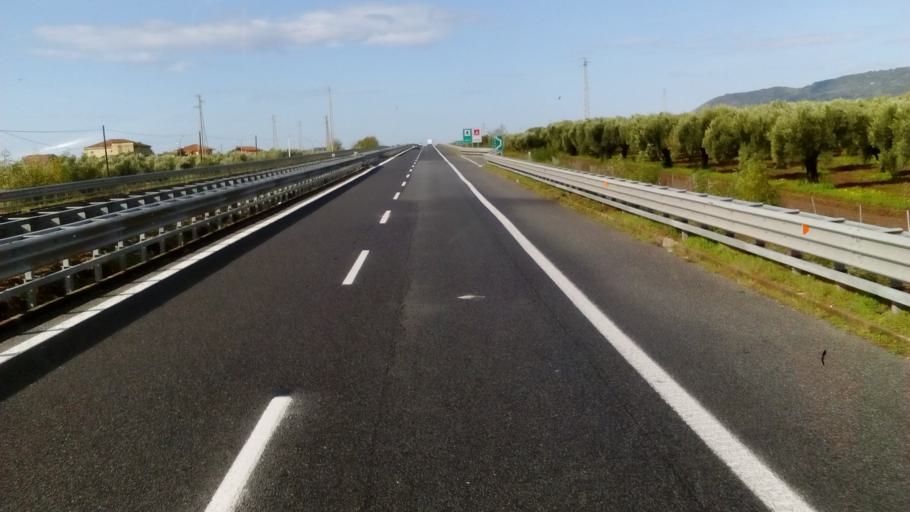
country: IT
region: Calabria
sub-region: Provincia di Catanzaro
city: Santa Eufemia Lamezia
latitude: 38.9245
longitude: 16.2563
